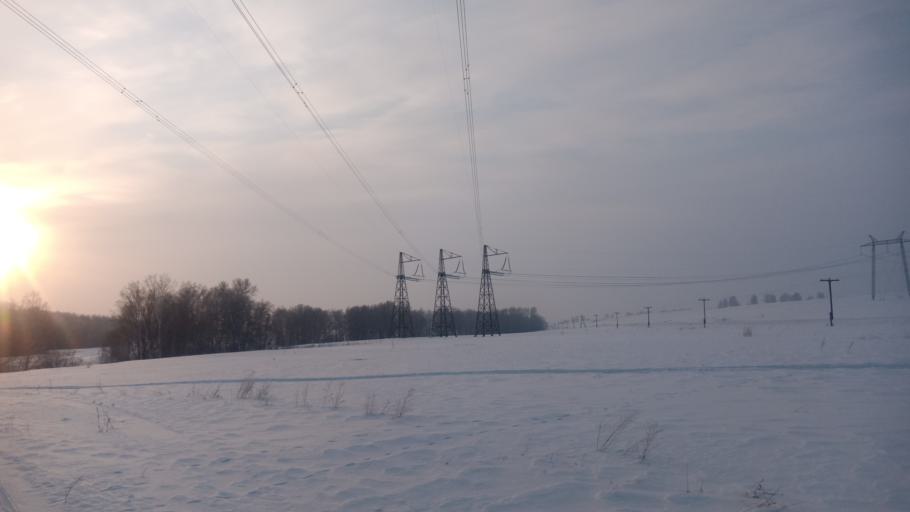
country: RU
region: Altai Krai
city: Nauchnyy Gorodok
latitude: 53.4057
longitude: 83.5144
